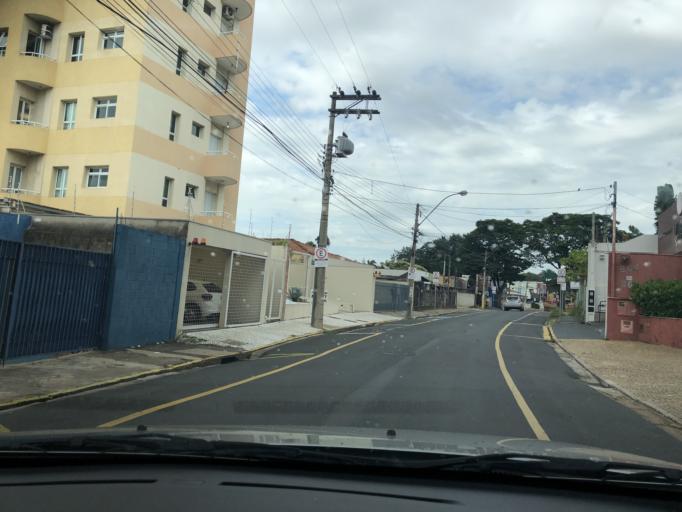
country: BR
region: Sao Paulo
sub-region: Americana
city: Americana
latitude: -22.7421
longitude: -47.3316
